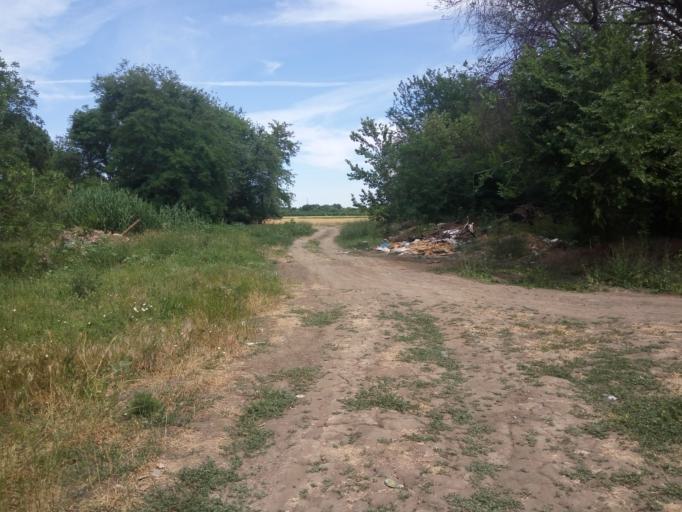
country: RU
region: Rostov
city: Bataysk
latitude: 47.1141
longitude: 39.7221
